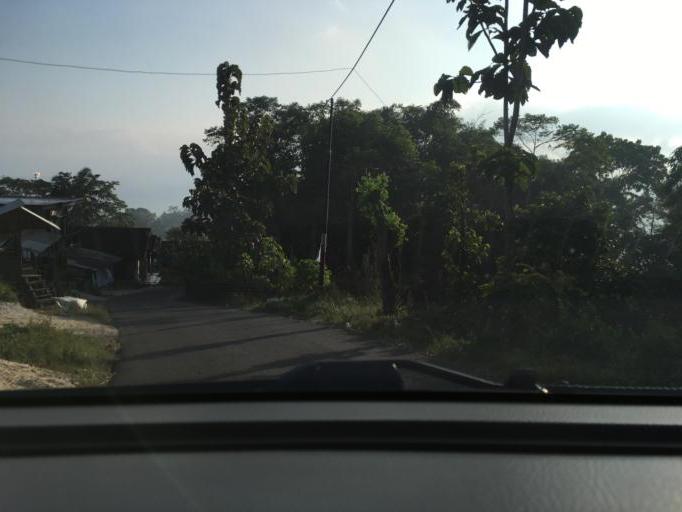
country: ID
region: West Java
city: Maniis
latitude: -7.0435
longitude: 108.3132
